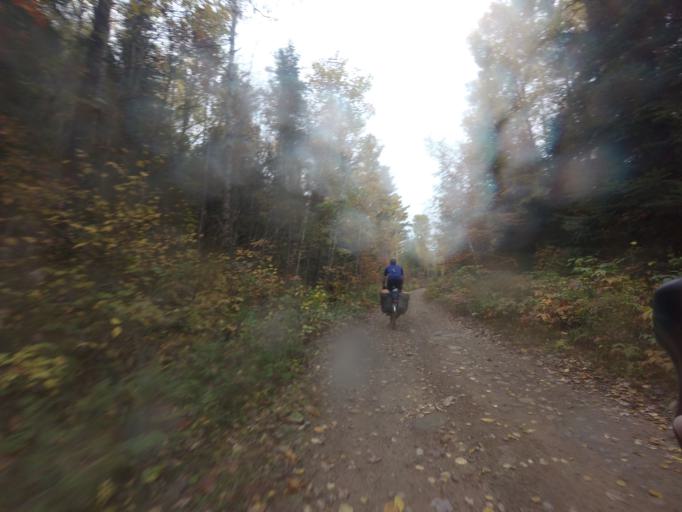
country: CA
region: Ontario
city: Petawawa
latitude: 45.7852
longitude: -77.3811
